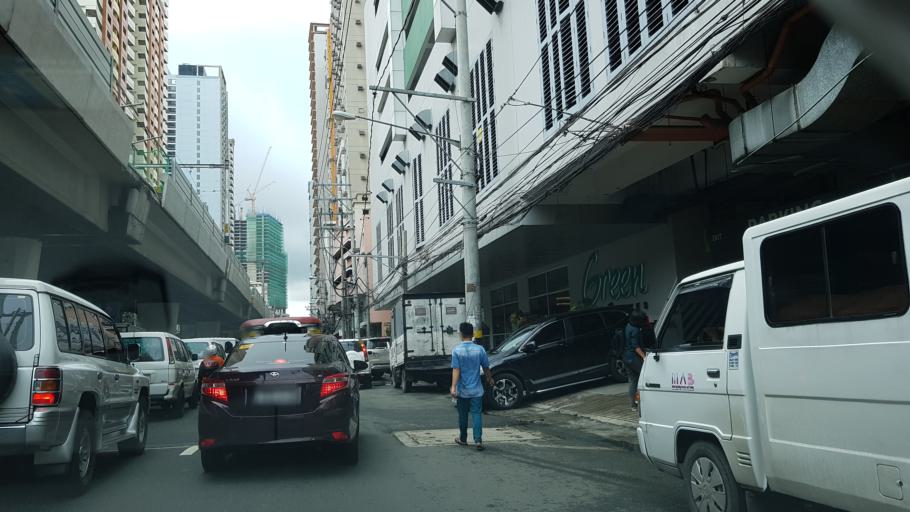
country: PH
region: Metro Manila
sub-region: City of Manila
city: Port Area
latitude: 14.5679
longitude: 120.9927
